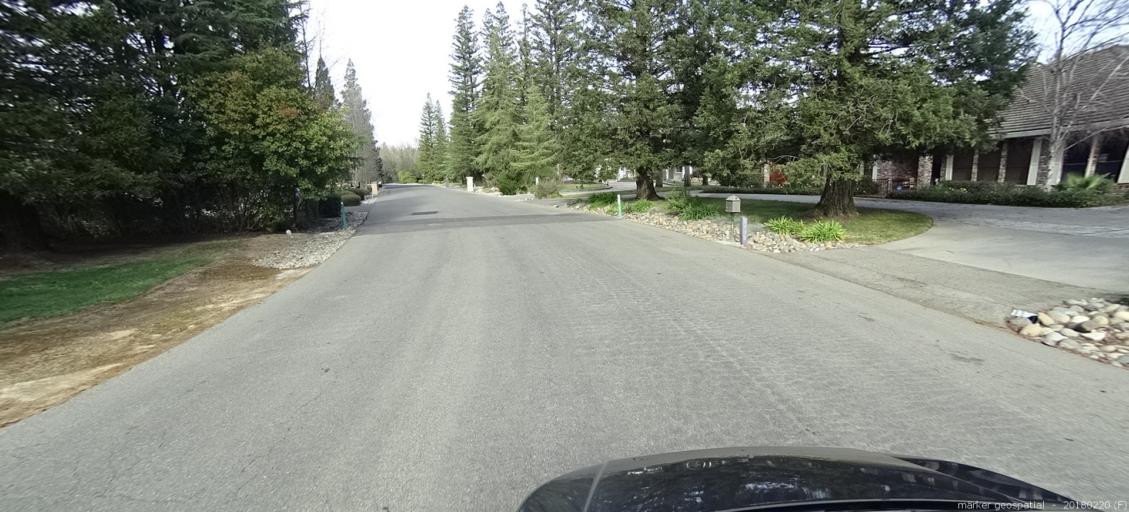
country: US
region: California
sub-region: Sacramento County
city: Orangevale
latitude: 38.7166
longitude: -121.2337
